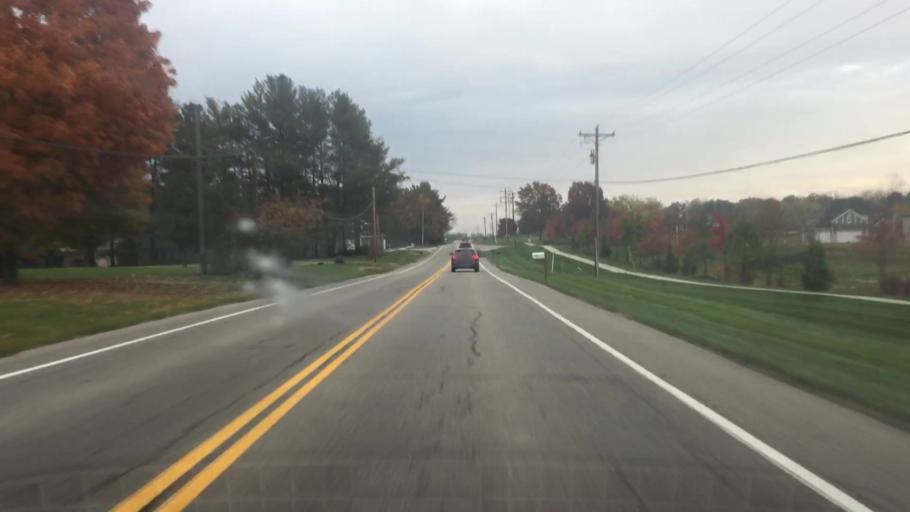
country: US
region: Missouri
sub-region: Boone County
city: Columbia
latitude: 38.8870
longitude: -92.3409
